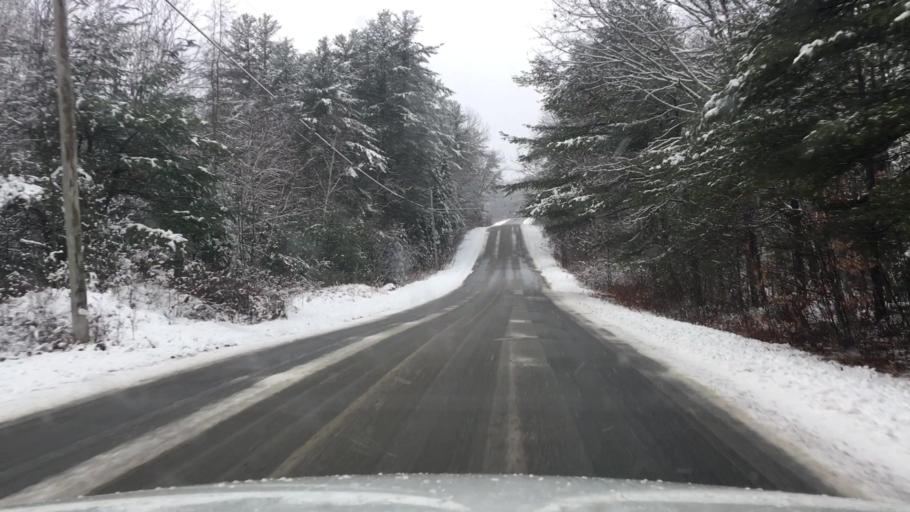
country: US
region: Maine
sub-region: Knox County
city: Union
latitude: 44.1685
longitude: -69.3209
